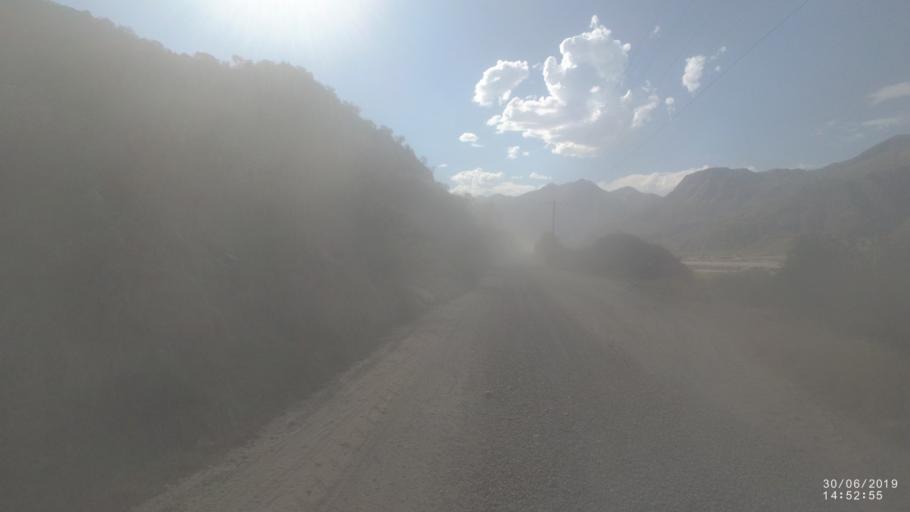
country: BO
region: Cochabamba
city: Irpa Irpa
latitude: -17.7669
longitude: -66.3478
